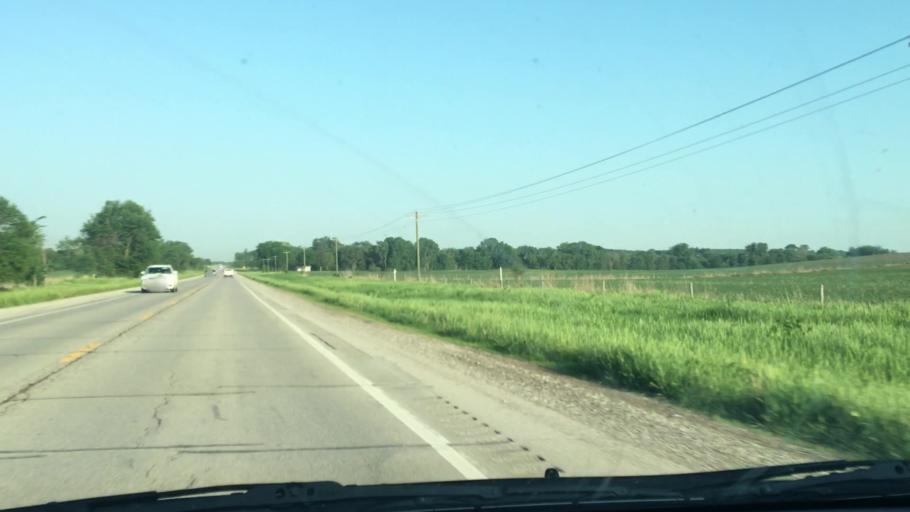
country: US
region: Iowa
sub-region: Johnson County
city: Tiffin
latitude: 41.7134
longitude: -91.7034
